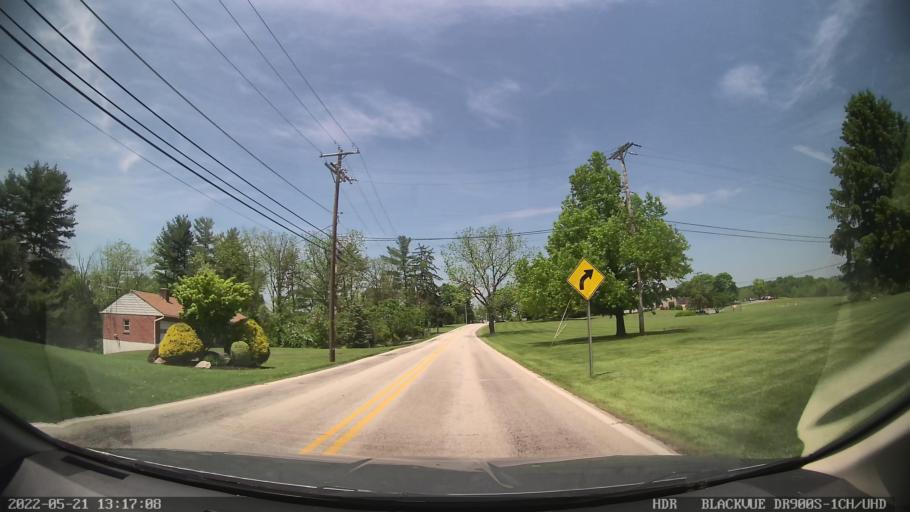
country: US
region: Pennsylvania
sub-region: Montgomery County
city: Gilbertsville
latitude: 40.3559
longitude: -75.5904
